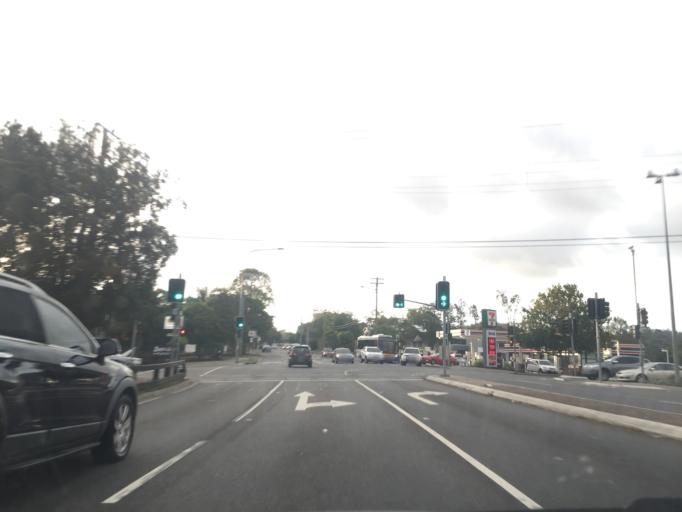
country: AU
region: Queensland
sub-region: Moreton Bay
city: Ferny Hills
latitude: -27.4433
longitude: 152.9444
